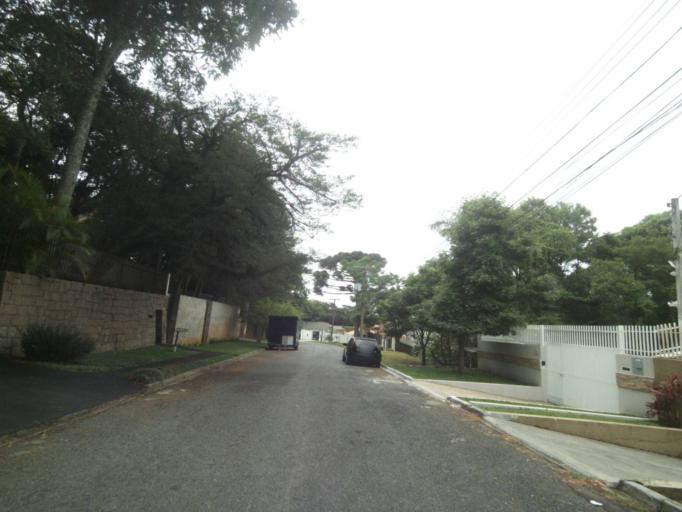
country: BR
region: Parana
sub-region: Curitiba
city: Curitiba
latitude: -25.4138
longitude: -49.3025
